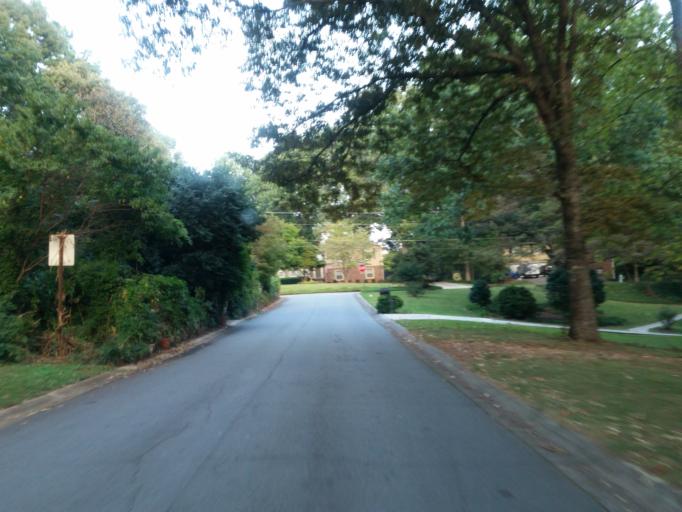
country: US
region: Georgia
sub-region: Cherokee County
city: Woodstock
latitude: 34.0208
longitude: -84.4740
